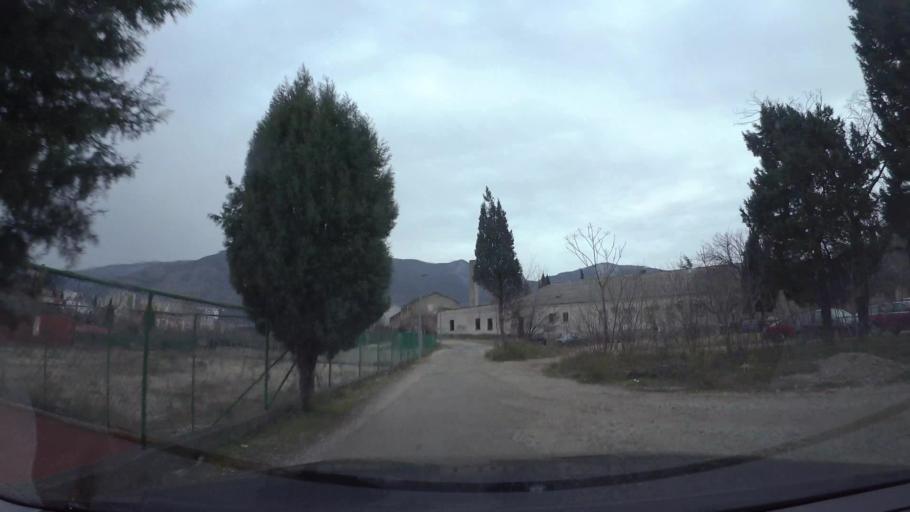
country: BA
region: Federation of Bosnia and Herzegovina
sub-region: Hercegovacko-Bosanski Kanton
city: Mostar
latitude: 43.3520
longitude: 17.8104
